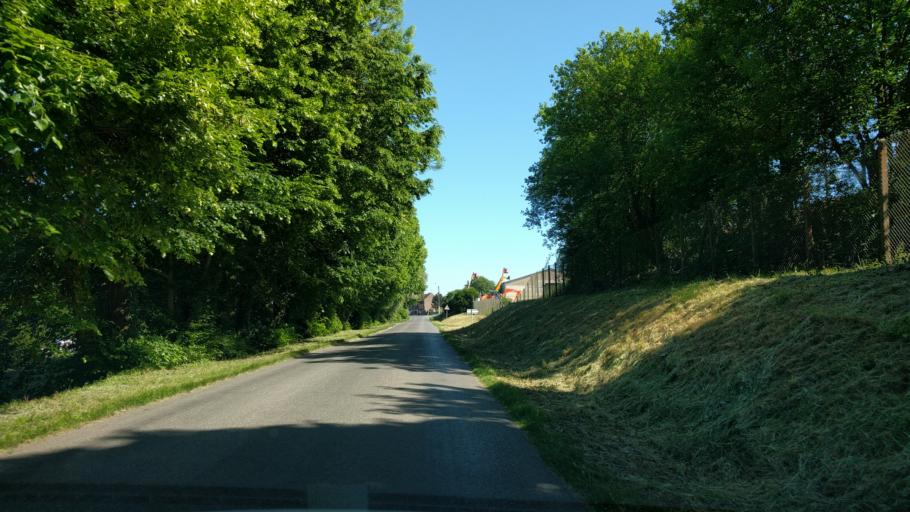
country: FR
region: Picardie
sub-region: Departement de la Somme
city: Peronne
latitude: 49.9181
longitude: 2.9301
